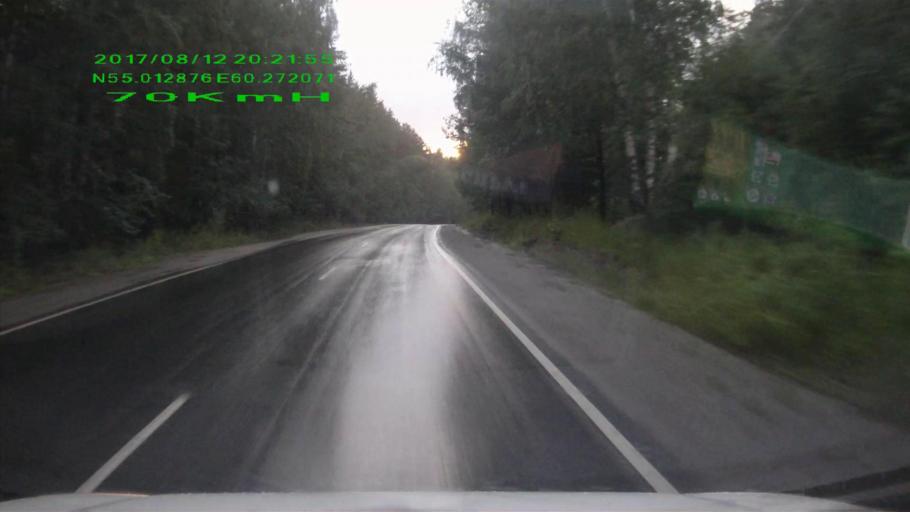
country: RU
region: Chelyabinsk
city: Chebarkul'
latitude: 55.0129
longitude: 60.2719
